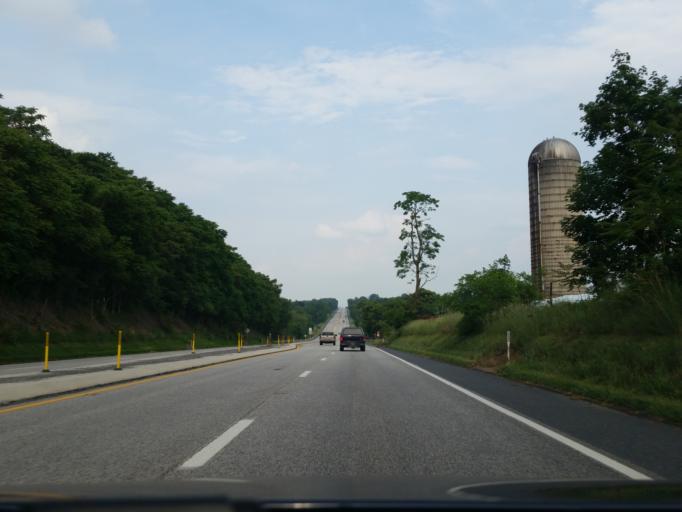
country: US
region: Pennsylvania
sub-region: Lebanon County
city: Jonestown
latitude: 40.4071
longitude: -76.5582
